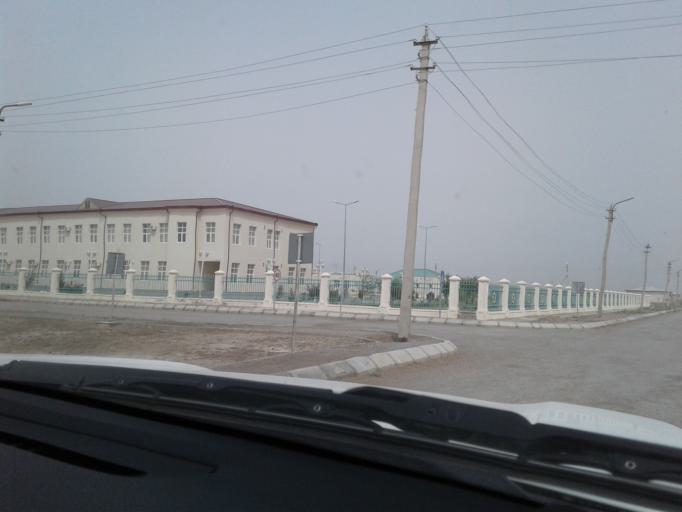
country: TM
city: Akdepe
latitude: 41.6333
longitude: 58.6647
